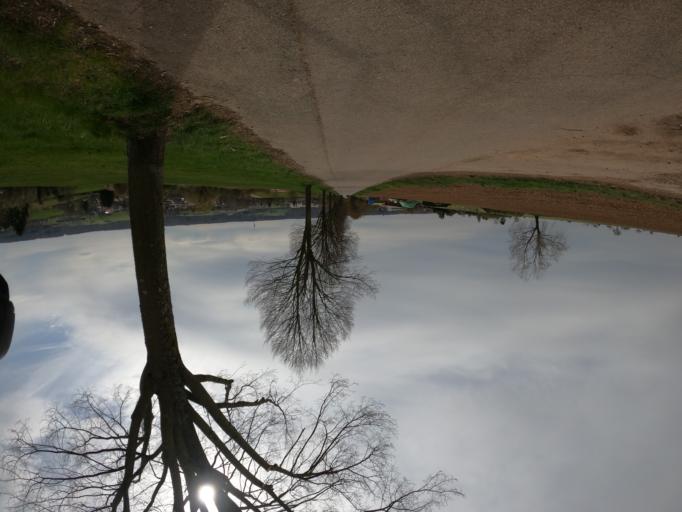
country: DE
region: Baden-Wuerttemberg
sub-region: Regierungsbezirk Stuttgart
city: Waldenbuch
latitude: 48.6489
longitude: 9.1359
